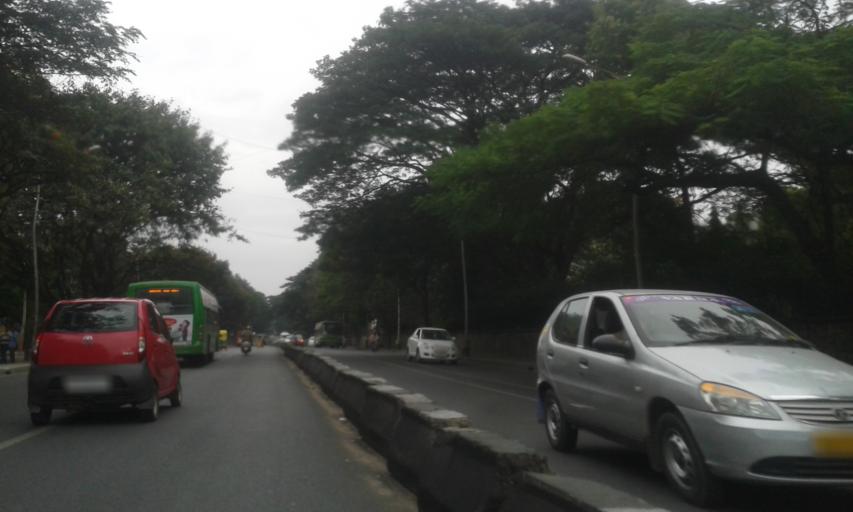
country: IN
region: Karnataka
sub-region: Bangalore Urban
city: Bangalore
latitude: 12.9267
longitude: 77.6229
